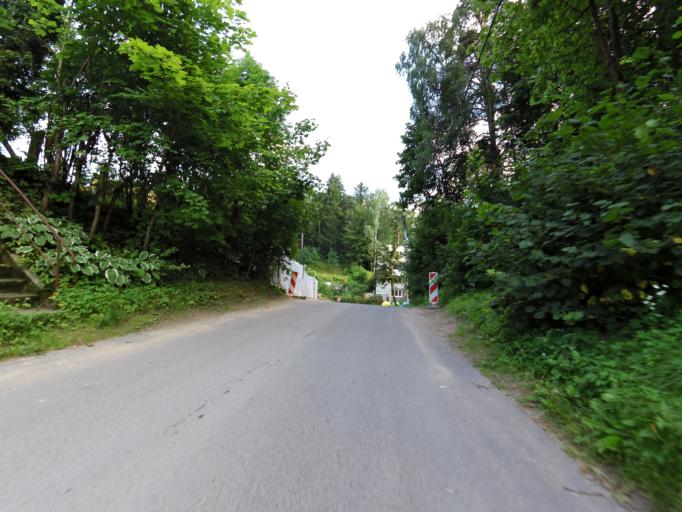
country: LT
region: Vilnius County
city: Rasos
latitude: 54.6963
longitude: 25.3178
